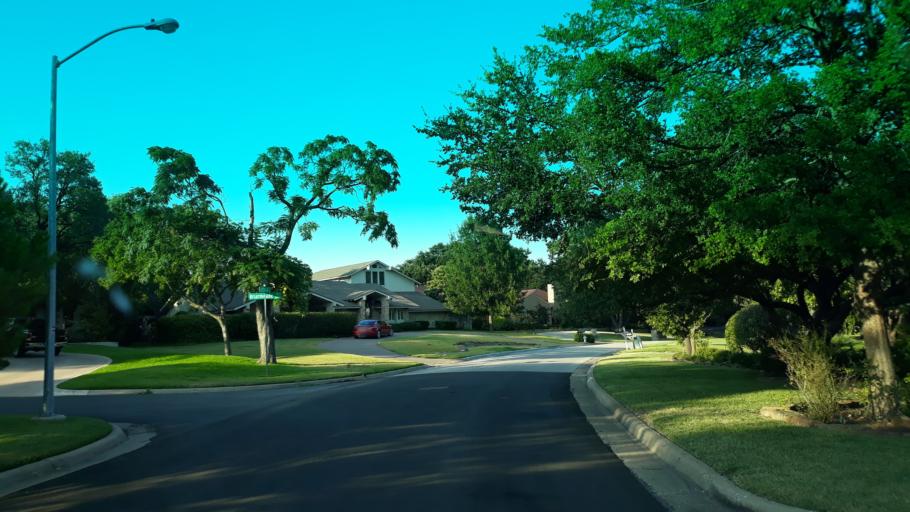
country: US
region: Texas
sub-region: Dallas County
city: Addison
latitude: 32.9490
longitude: -96.7886
